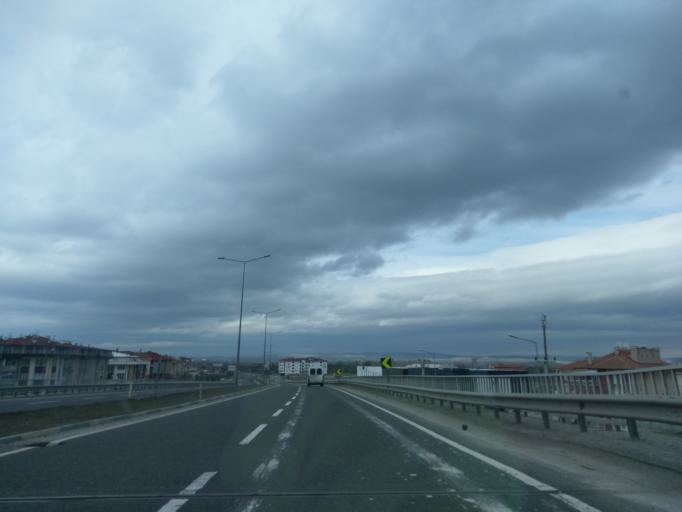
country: TR
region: Kuetahya
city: Kutahya
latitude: 39.4055
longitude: 30.0285
